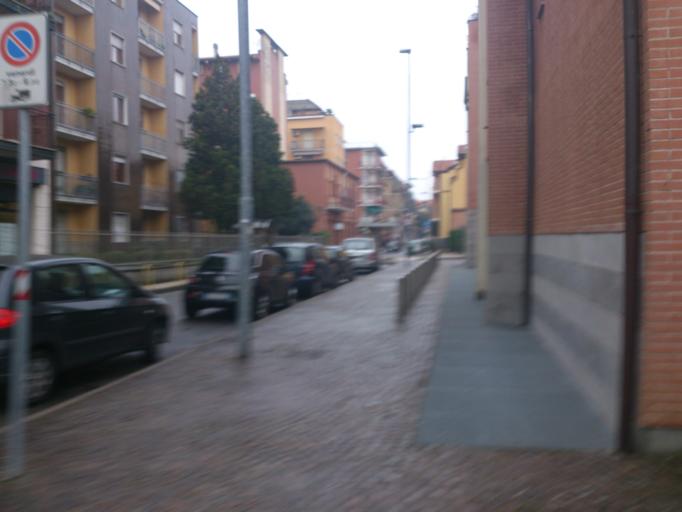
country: IT
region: Lombardy
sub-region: Citta metropolitana di Milano
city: Civesio
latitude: 45.4075
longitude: 9.2699
